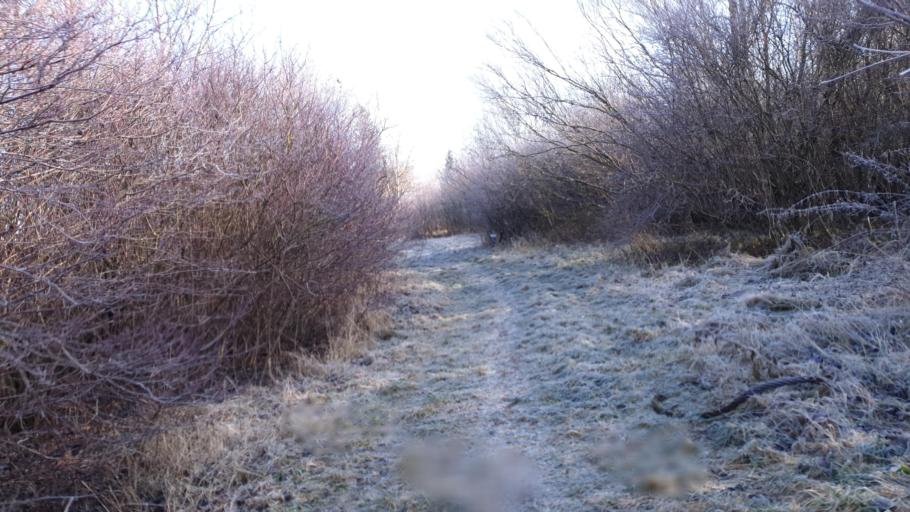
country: DE
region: Bavaria
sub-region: Upper Bavaria
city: Pasing
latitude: 48.1429
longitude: 11.4359
